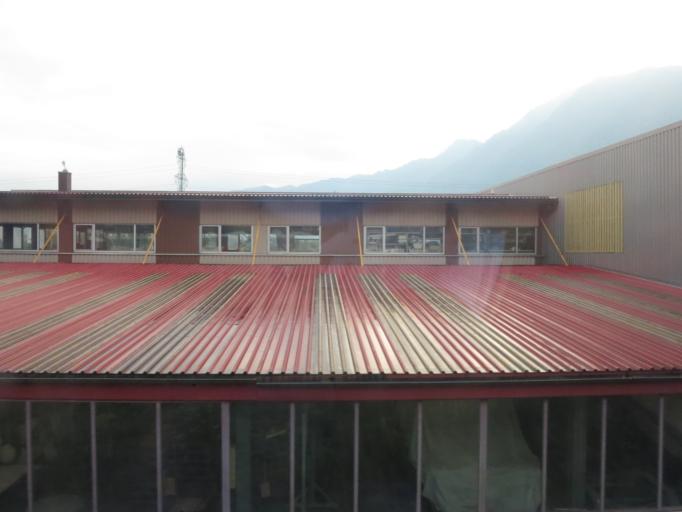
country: CH
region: Glarus
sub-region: Glarus
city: Bilten
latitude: 47.1516
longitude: 9.0313
